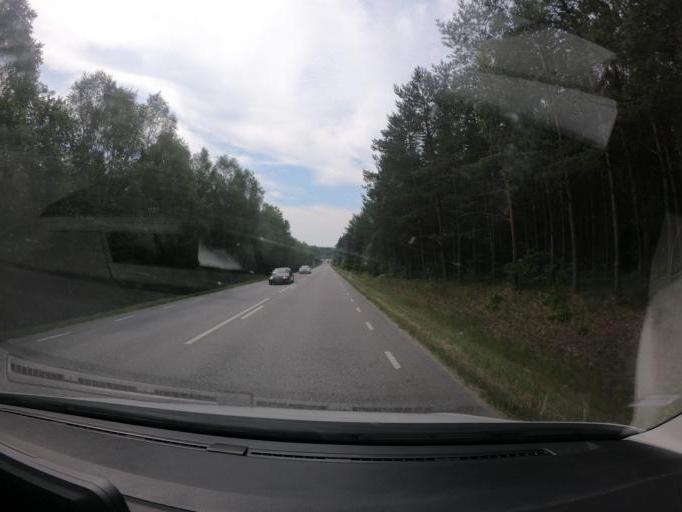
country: SE
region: Skane
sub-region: Hassleholms Kommun
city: Bjarnum
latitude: 56.2402
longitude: 13.7136
